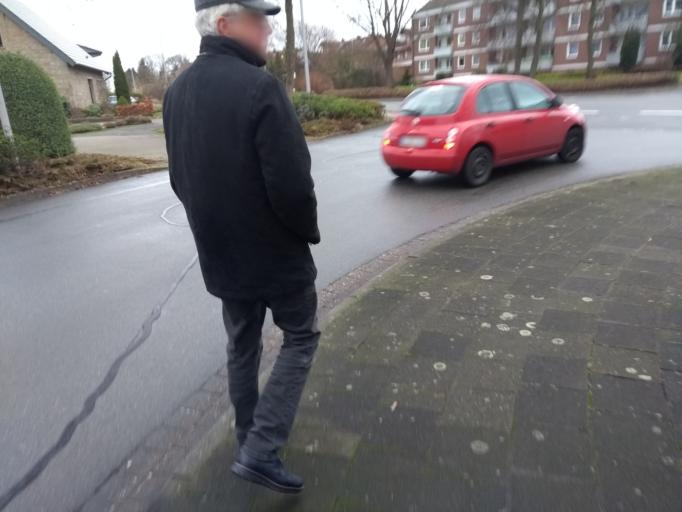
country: DE
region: North Rhine-Westphalia
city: Ibbenburen
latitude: 52.2829
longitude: 7.7018
